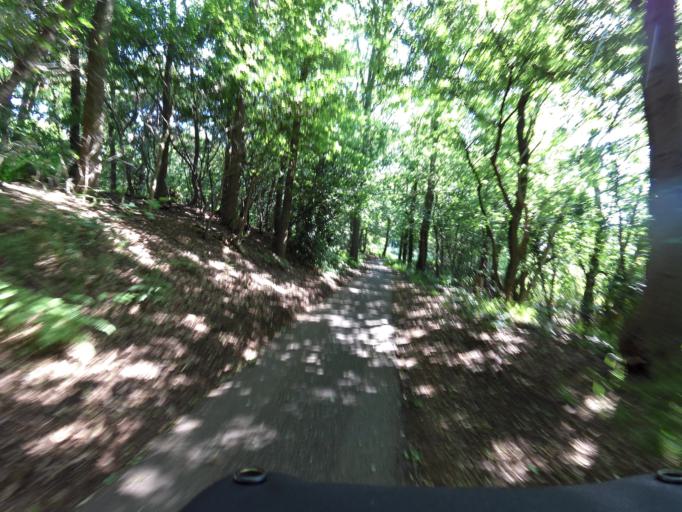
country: NL
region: Overijssel
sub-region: Gemeente Dalfsen
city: Dalfsen
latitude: 52.5268
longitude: 6.3557
